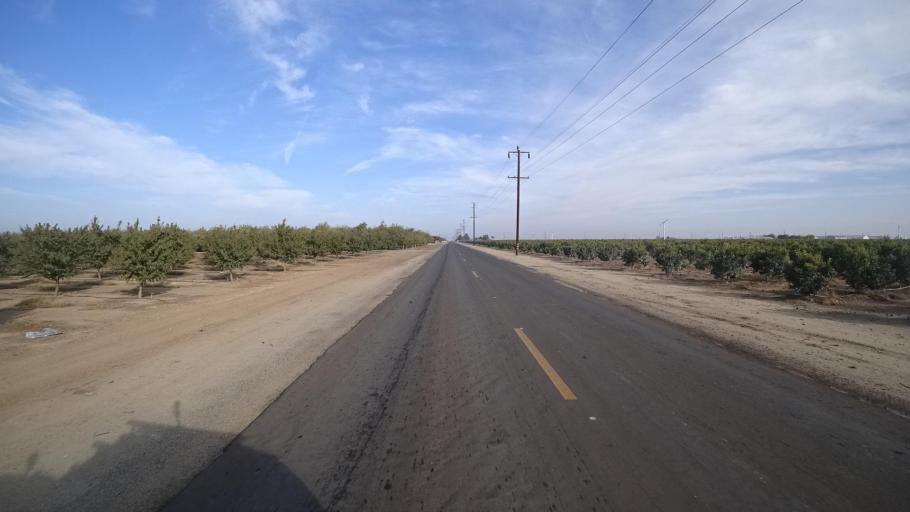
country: US
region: California
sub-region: Kern County
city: Delano
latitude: 35.7700
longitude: -119.2053
